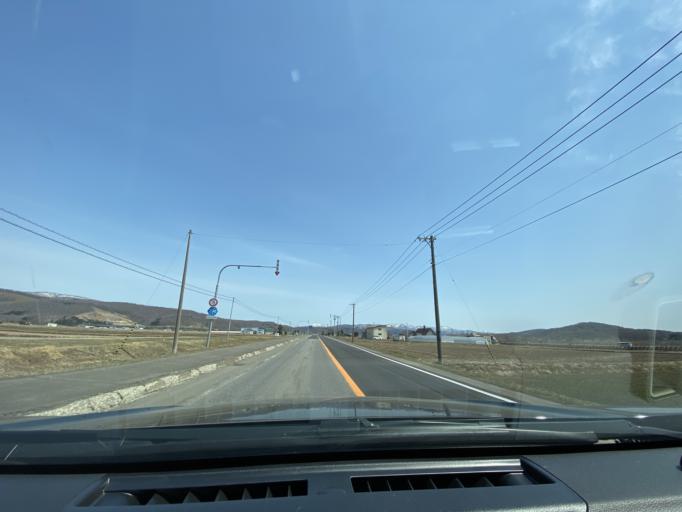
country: JP
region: Hokkaido
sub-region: Asahikawa-shi
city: Asahikawa
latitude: 43.8969
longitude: 142.5189
